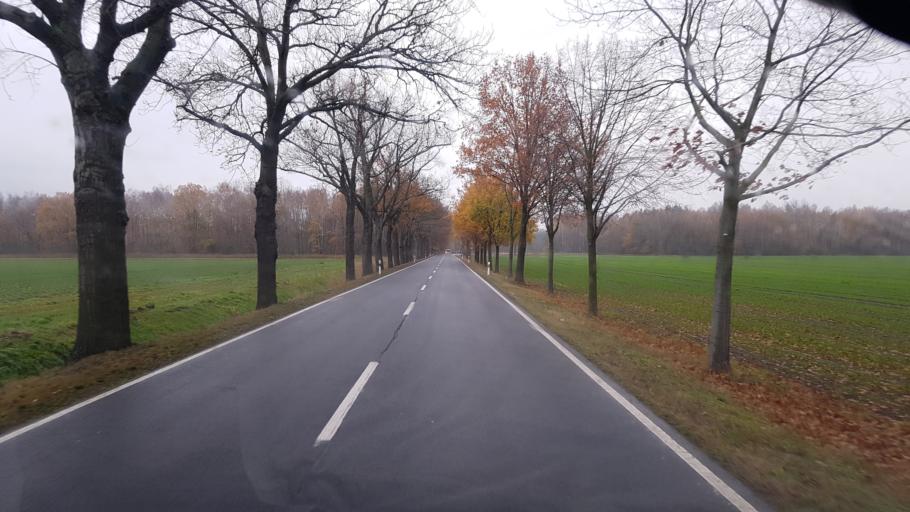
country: DE
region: Brandenburg
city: Schraden
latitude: 51.4469
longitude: 13.7109
